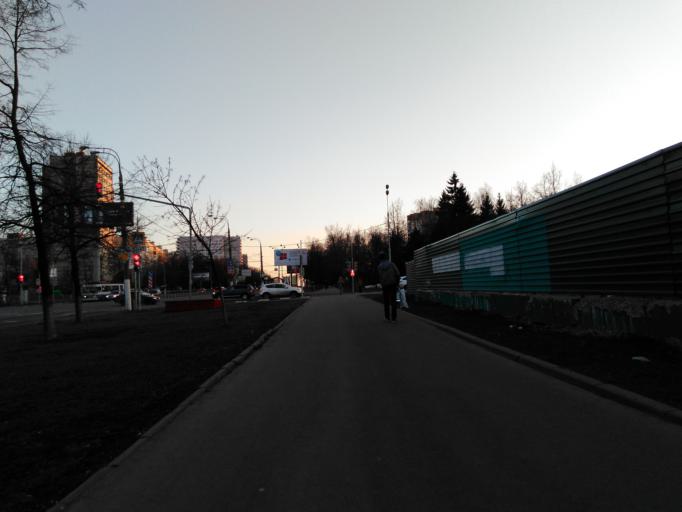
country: RU
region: Moskovskaya
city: Cheremushki
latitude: 55.6509
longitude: 37.5333
